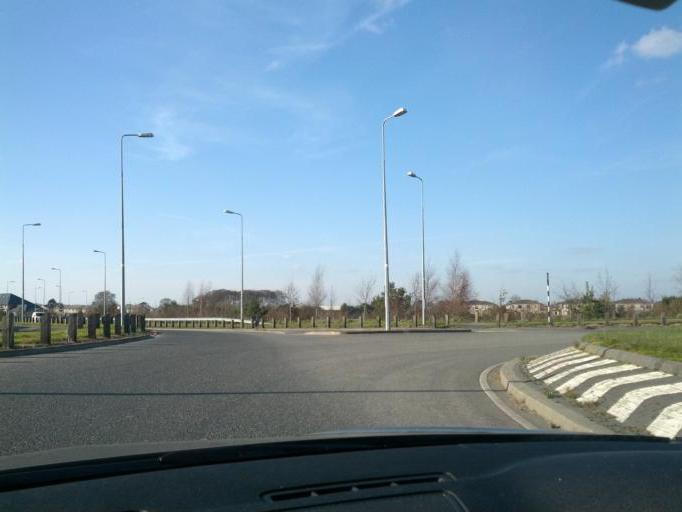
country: IE
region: Leinster
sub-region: Kildare
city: Naas
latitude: 53.2090
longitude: -6.6774
